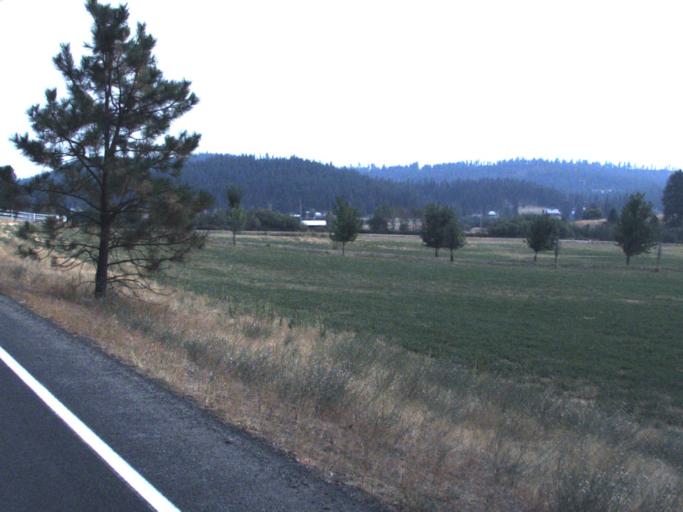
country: US
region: Washington
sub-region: Spokane County
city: Trentwood
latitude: 47.8137
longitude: -117.2140
